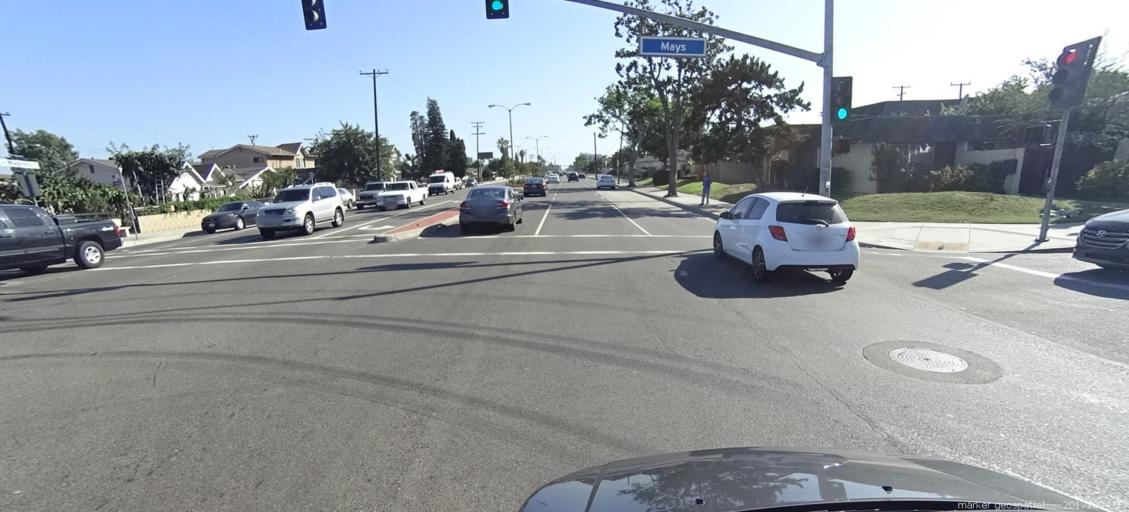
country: US
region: California
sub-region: Orange County
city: Midway City
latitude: 33.7637
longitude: -117.9725
